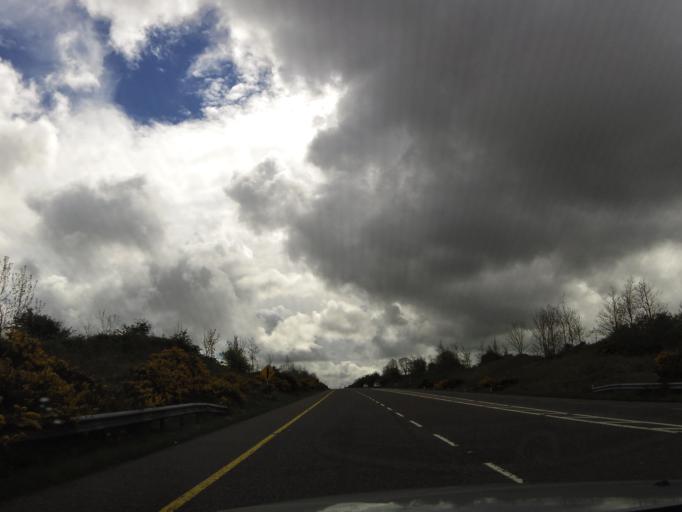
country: IE
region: Connaught
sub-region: Maigh Eo
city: Claremorris
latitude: 53.7682
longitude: -8.9576
